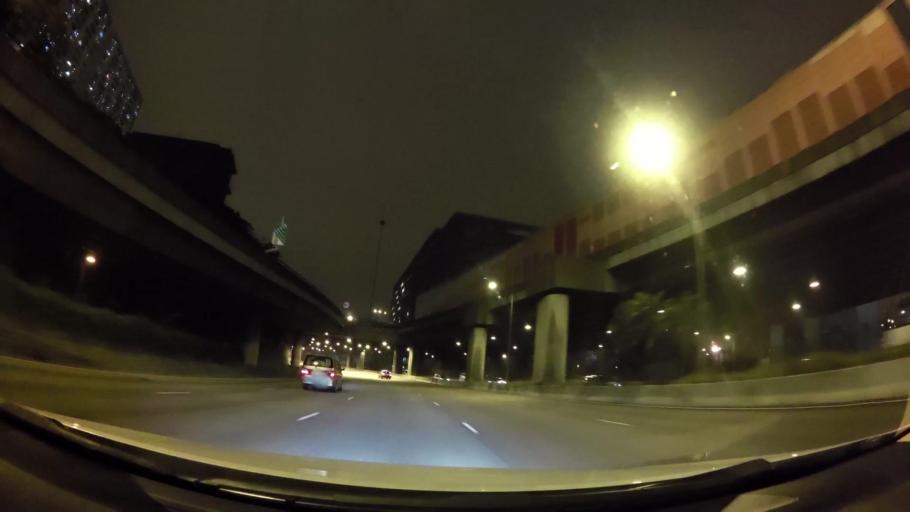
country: HK
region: Tsuen Wan
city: Tsuen Wan
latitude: 22.3464
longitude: 114.1250
